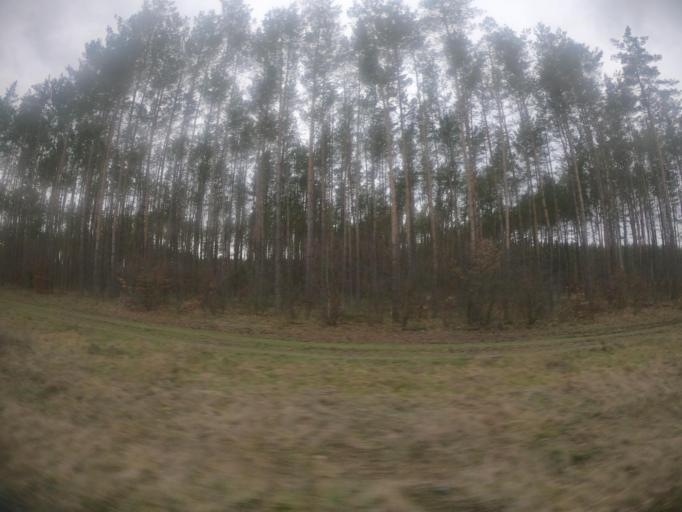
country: PL
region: West Pomeranian Voivodeship
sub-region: Powiat szczecinecki
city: Bialy Bor
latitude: 53.7783
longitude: 16.8568
